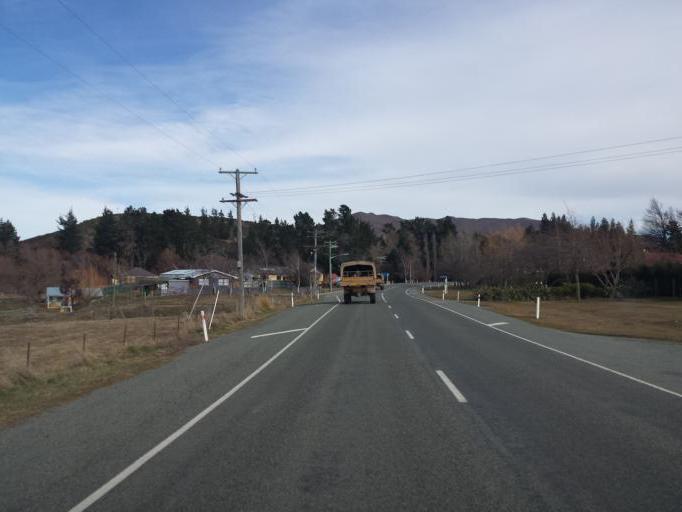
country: NZ
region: Canterbury
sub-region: Timaru District
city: Pleasant Point
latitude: -44.0884
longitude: 170.6539
